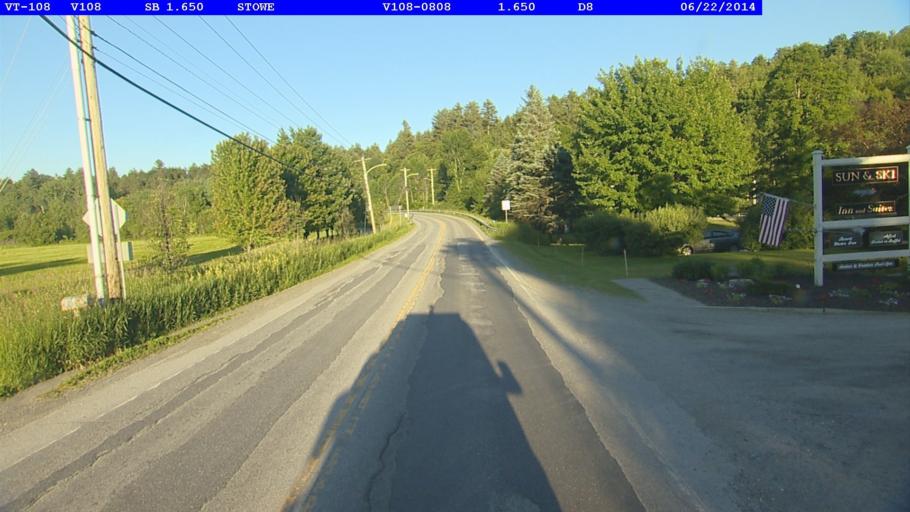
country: US
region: Vermont
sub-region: Lamoille County
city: Morristown
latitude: 44.4728
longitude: -72.7090
